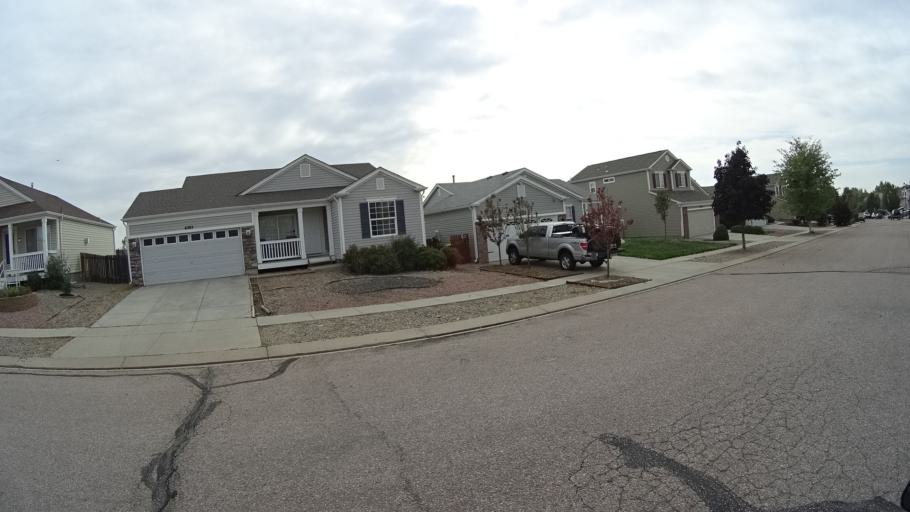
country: US
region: Colorado
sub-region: El Paso County
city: Cimarron Hills
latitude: 38.9250
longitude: -104.7048
